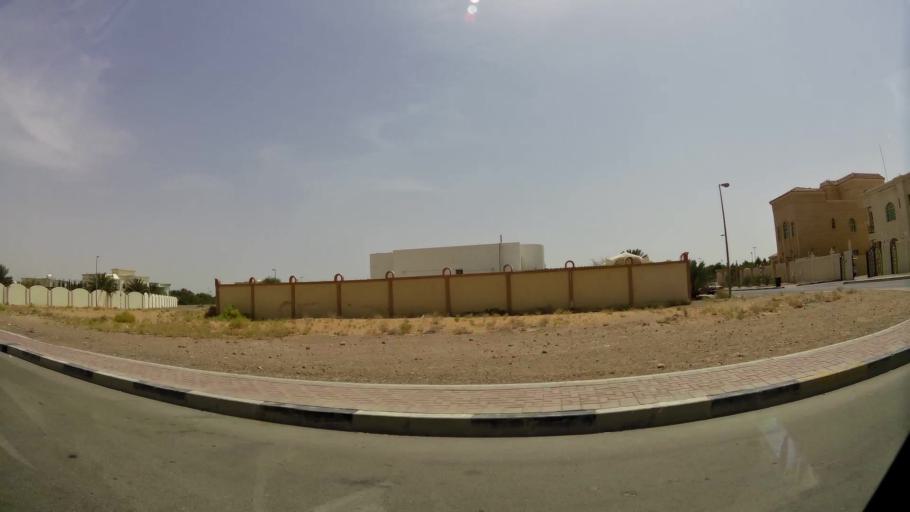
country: AE
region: Abu Dhabi
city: Al Ain
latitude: 24.1711
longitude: 55.7125
